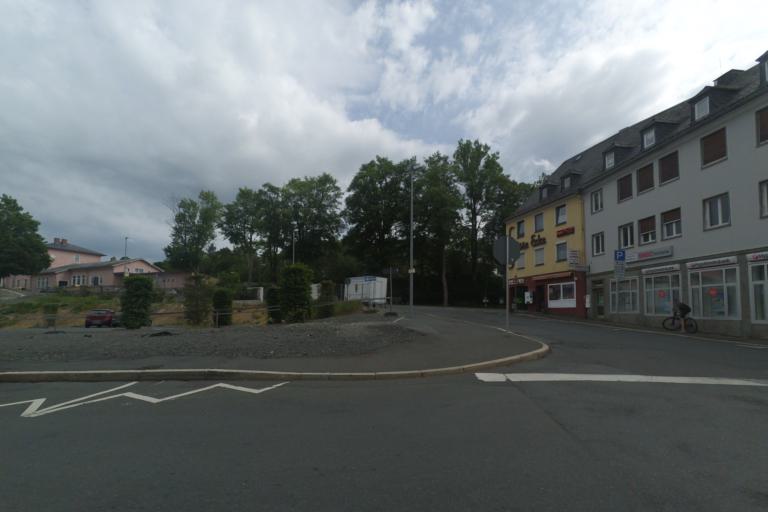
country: DE
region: Bavaria
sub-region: Upper Franconia
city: Munchberg
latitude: 50.1898
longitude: 11.7894
